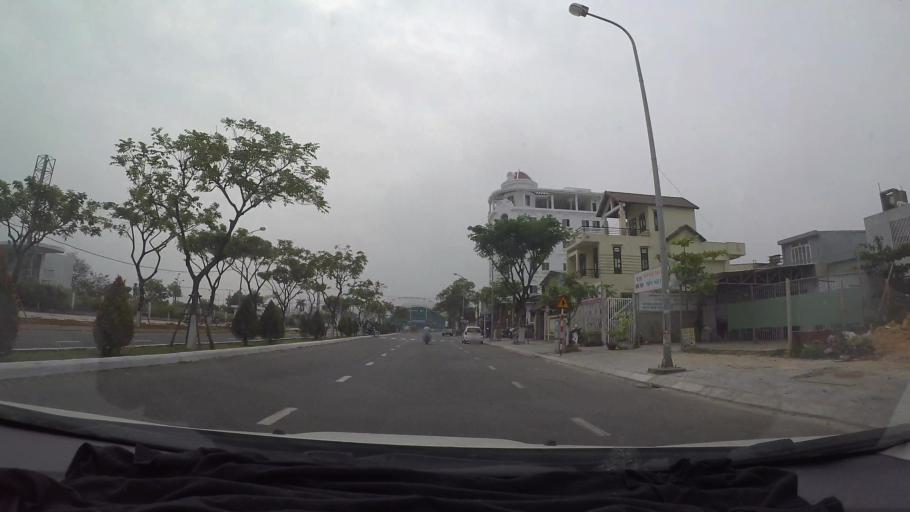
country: VN
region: Da Nang
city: Cam Le
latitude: 16.0246
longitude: 108.2156
